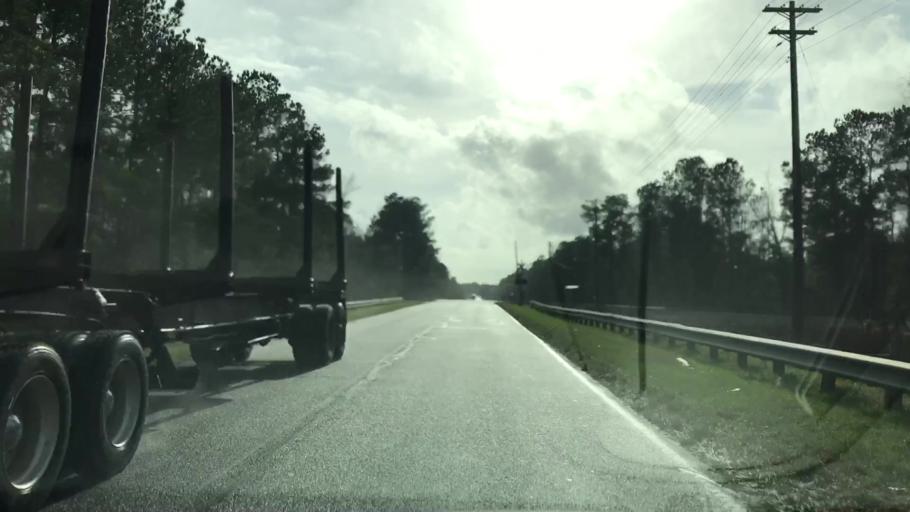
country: US
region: South Carolina
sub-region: Williamsburg County
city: Andrews
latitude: 33.4843
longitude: -79.5521
